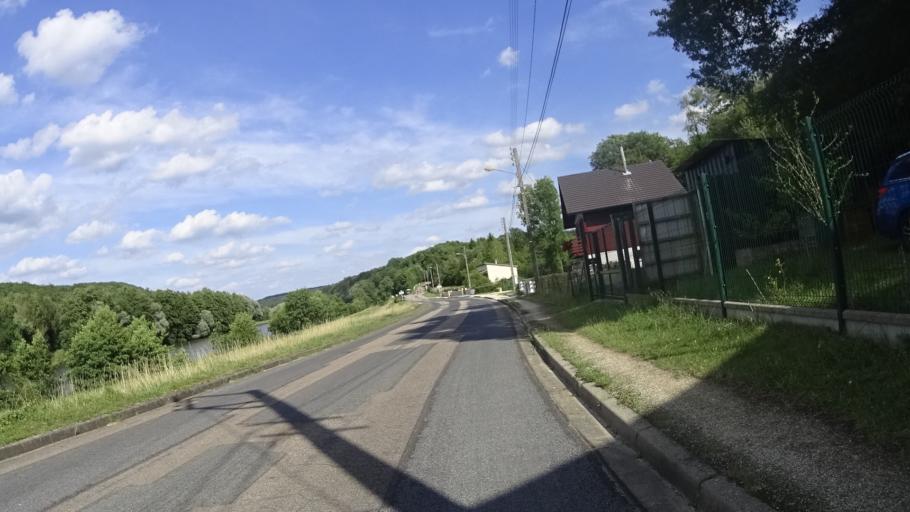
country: FR
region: Lorraine
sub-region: Departement de Meurthe-et-Moselle
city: Dommartin-les-Toul
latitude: 48.6432
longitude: 5.9394
